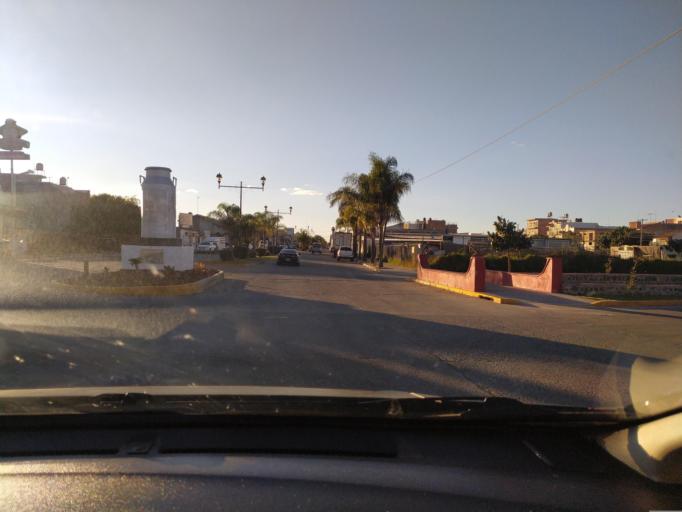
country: MX
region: Jalisco
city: San Julian
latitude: 21.0086
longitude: -102.1703
